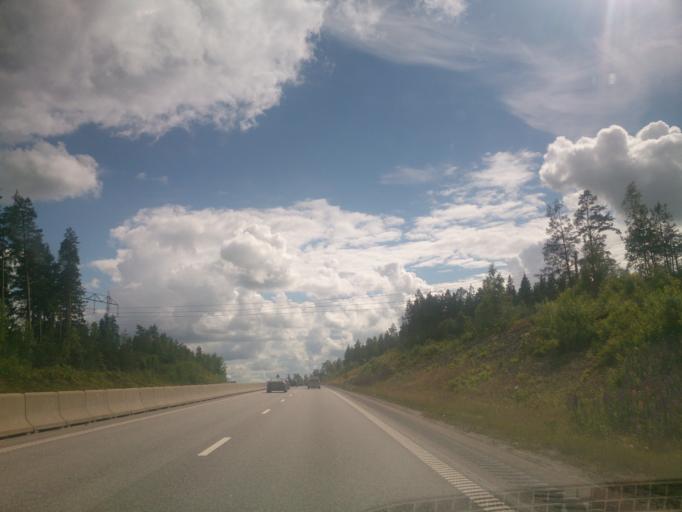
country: SE
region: OEstergoetland
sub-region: Norrkopings Kommun
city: Kimstad
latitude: 58.5163
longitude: 15.9969
